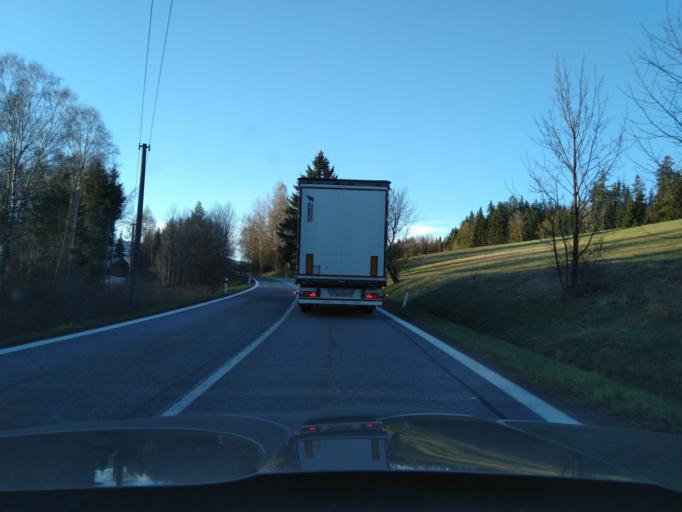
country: CZ
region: Jihocesky
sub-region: Okres Prachatice
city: Vimperk
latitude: 49.0242
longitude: 13.7664
